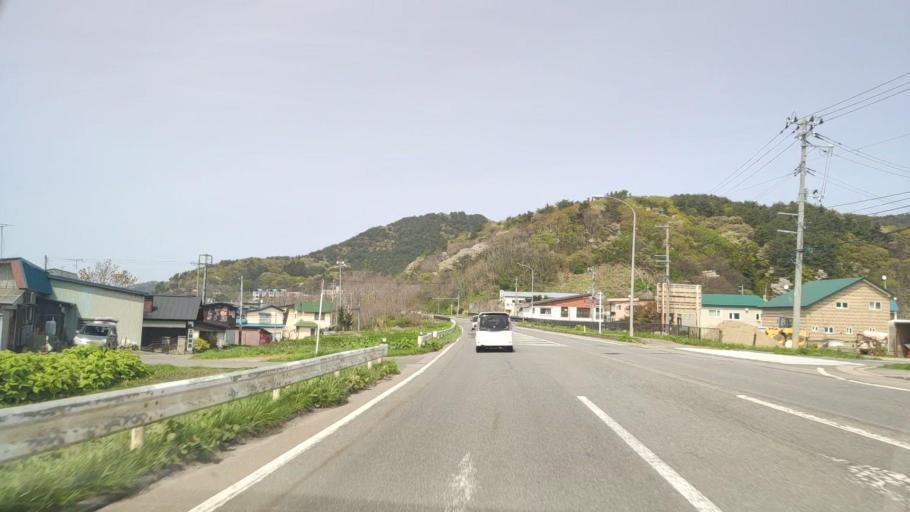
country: JP
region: Aomori
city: Aomori Shi
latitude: 40.8711
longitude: 140.8504
